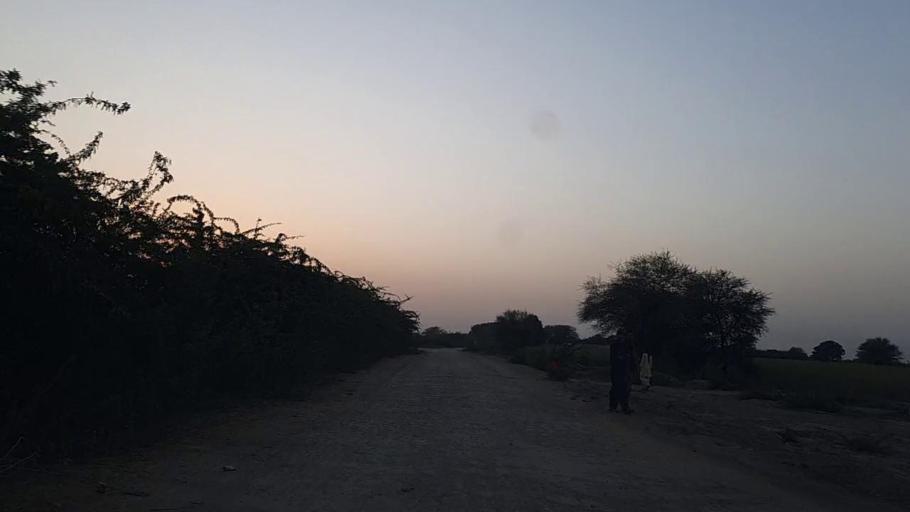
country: PK
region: Sindh
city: Naukot
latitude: 24.7487
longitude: 69.3123
